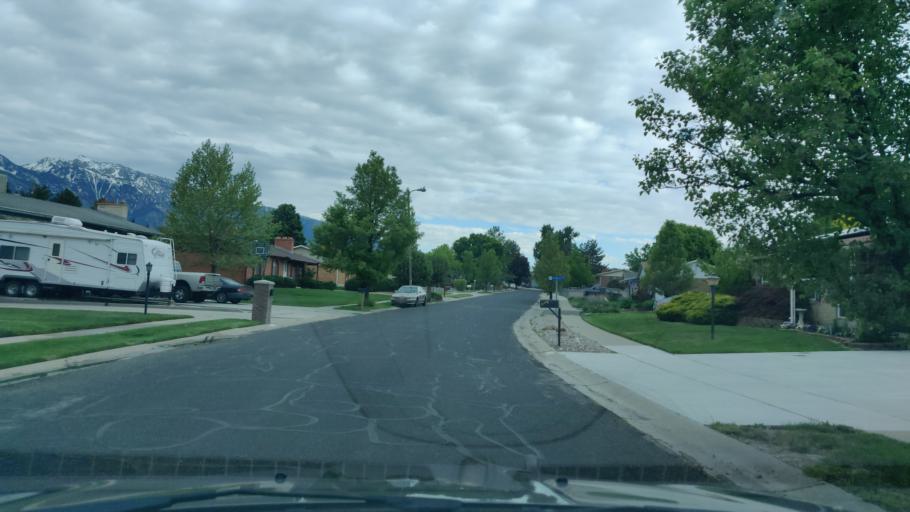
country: US
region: Utah
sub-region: Salt Lake County
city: Little Cottonwood Creek Valley
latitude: 40.6195
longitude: -111.8474
